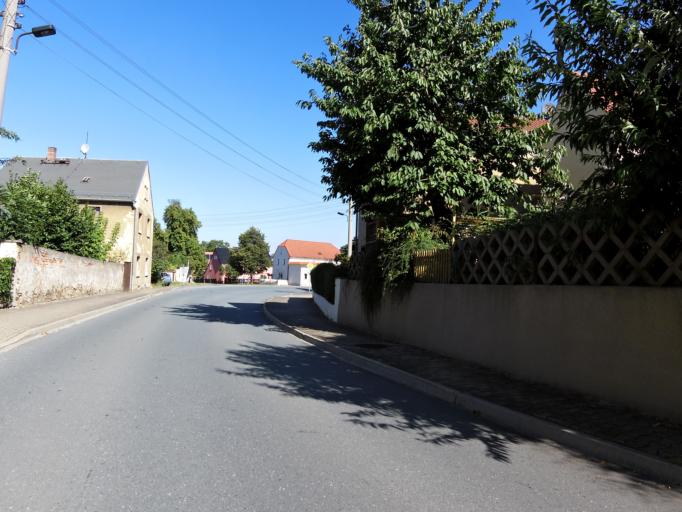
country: DE
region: Saxony
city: Riesa
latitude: 51.3241
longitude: 13.2989
